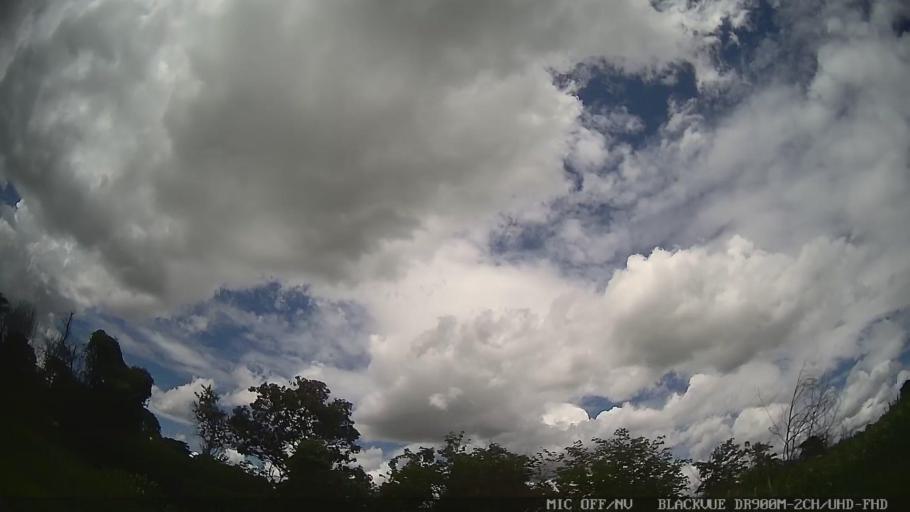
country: BR
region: Sao Paulo
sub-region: Jaguariuna
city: Jaguariuna
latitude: -22.7095
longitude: -46.9583
